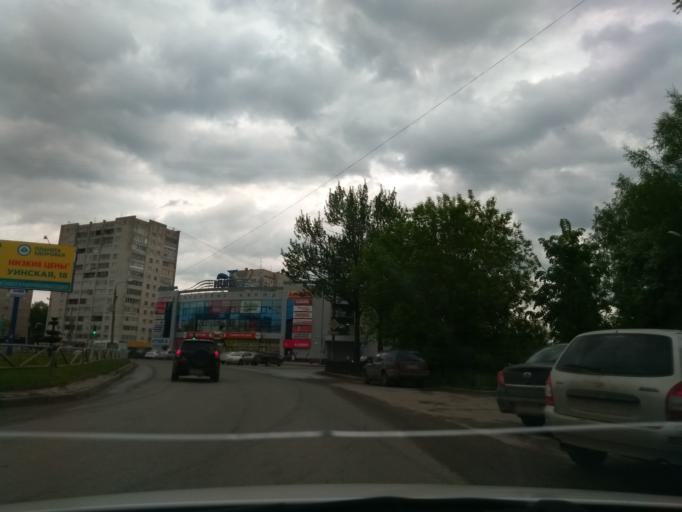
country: RU
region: Perm
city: Perm
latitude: 57.9976
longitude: 56.2923
